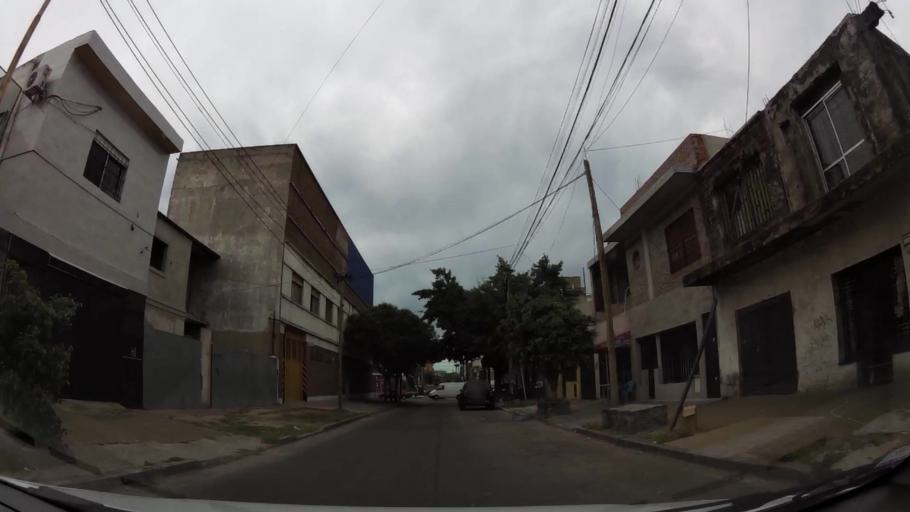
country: AR
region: Buenos Aires
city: San Justo
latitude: -34.6830
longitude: -58.5173
